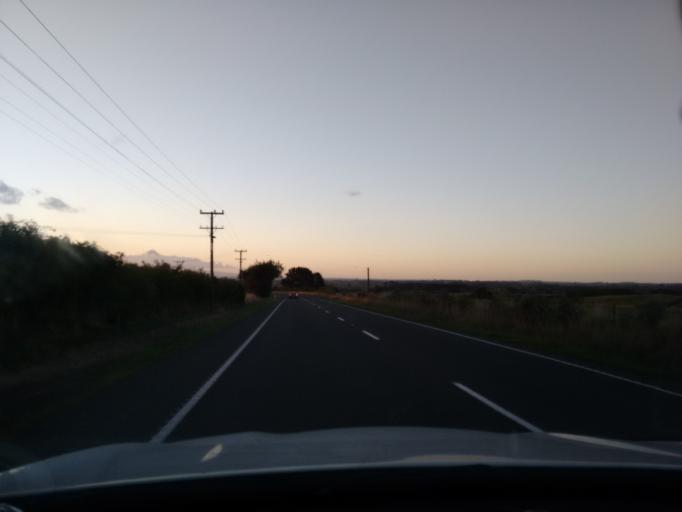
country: NZ
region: Taranaki
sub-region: South Taranaki District
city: Hawera
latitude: -39.6541
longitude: 174.3934
